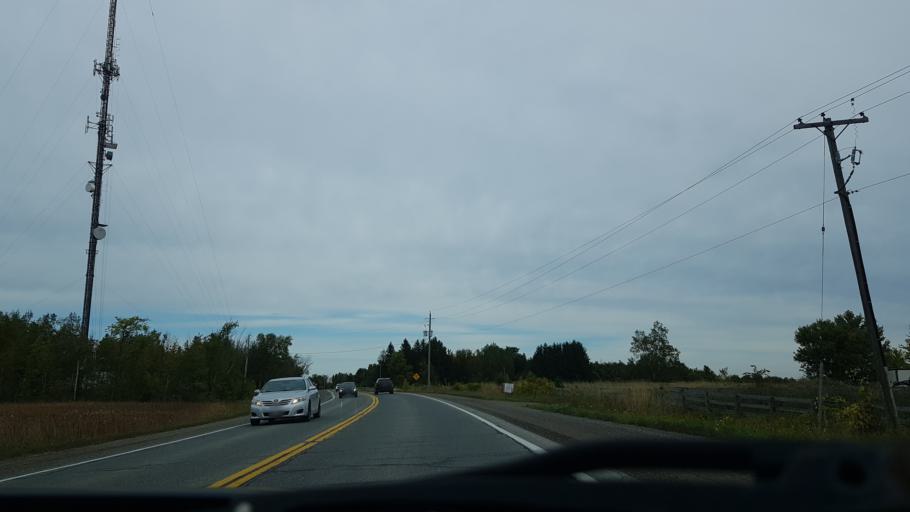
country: CA
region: Ontario
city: Orangeville
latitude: 43.9106
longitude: -79.9393
